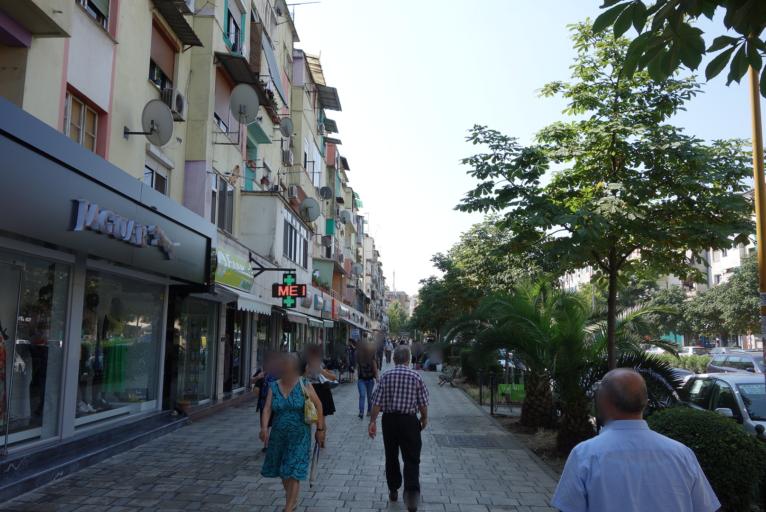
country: AL
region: Tirane
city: Tirana
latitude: 41.3234
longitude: 19.8047
